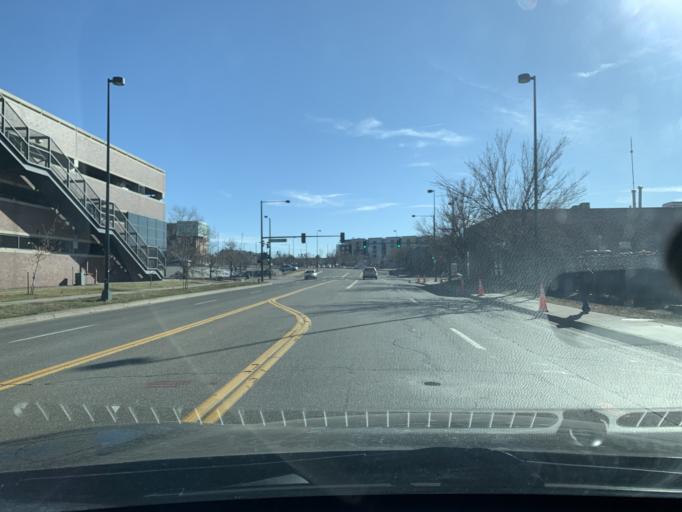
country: US
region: Colorado
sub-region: Denver County
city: Denver
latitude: 39.7428
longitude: -105.0079
